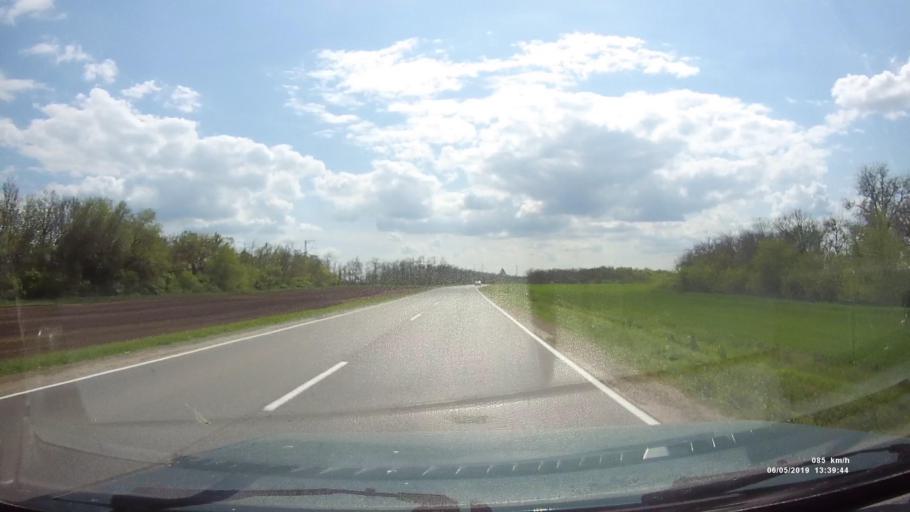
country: RU
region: Rostov
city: Ust'-Donetskiy
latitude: 47.6722
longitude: 40.7005
